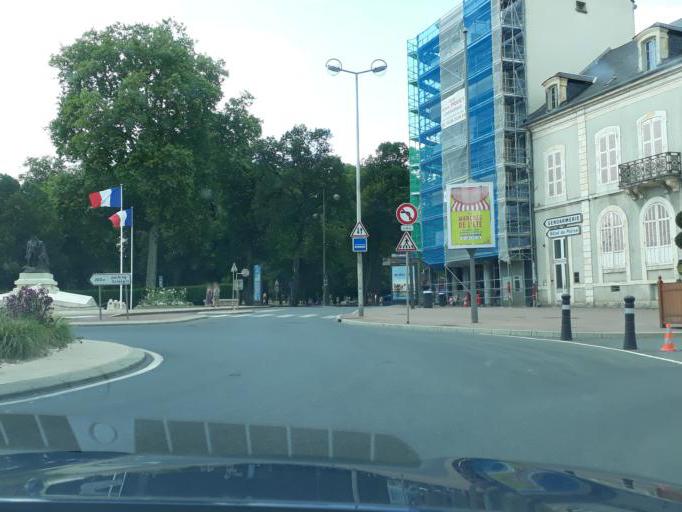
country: FR
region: Bourgogne
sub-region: Departement de la Nievre
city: Nevers
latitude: 46.9890
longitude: 3.1573
